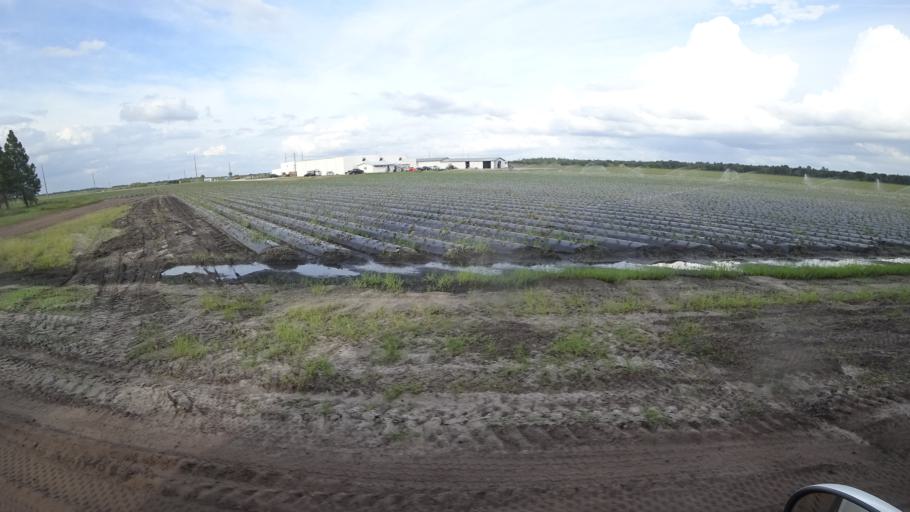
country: US
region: Florida
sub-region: Hillsborough County
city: Wimauma
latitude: 27.5839
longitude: -82.1593
